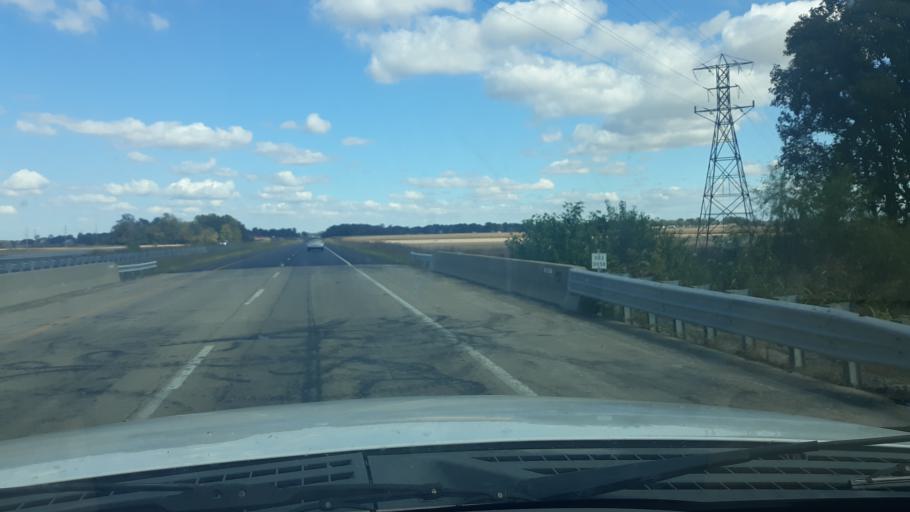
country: US
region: Illinois
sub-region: Saline County
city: Harrisburg
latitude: 37.7747
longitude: -88.5032
